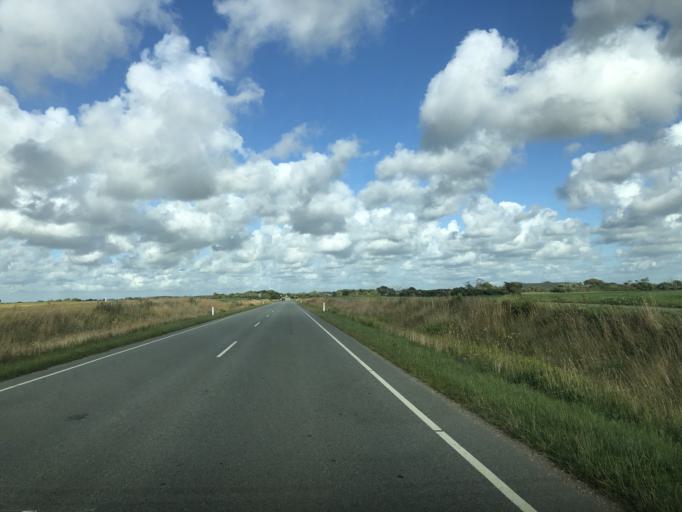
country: DK
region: Central Jutland
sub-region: Lemvig Kommune
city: Lemvig
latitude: 56.4926
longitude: 8.2214
